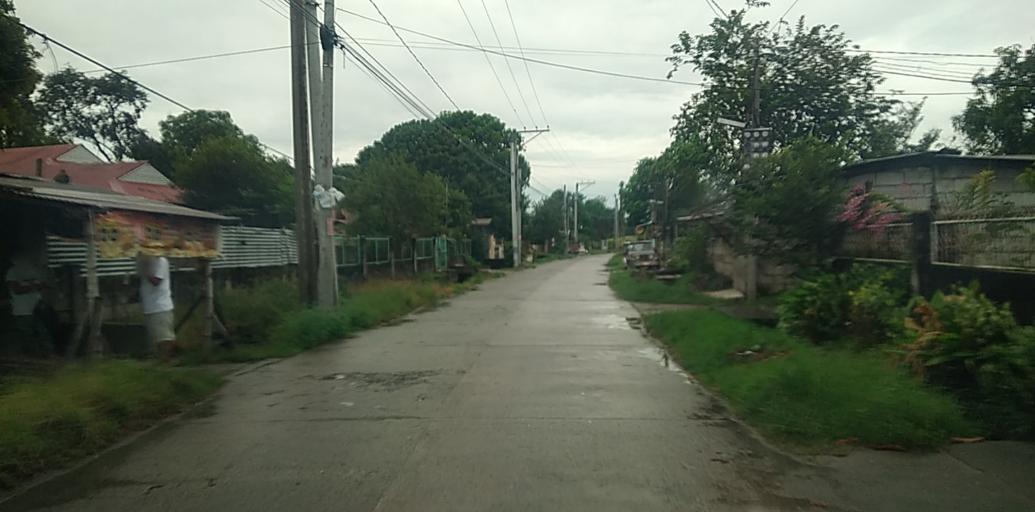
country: PH
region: Central Luzon
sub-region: Province of Pampanga
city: Arayat
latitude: 15.1462
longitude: 120.7411
